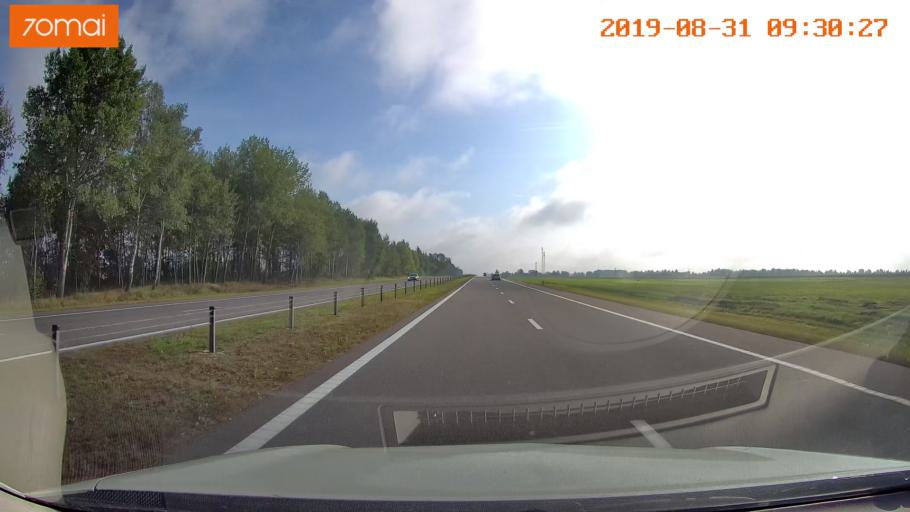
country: BY
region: Minsk
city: Byerazino
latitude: 53.8531
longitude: 29.1240
